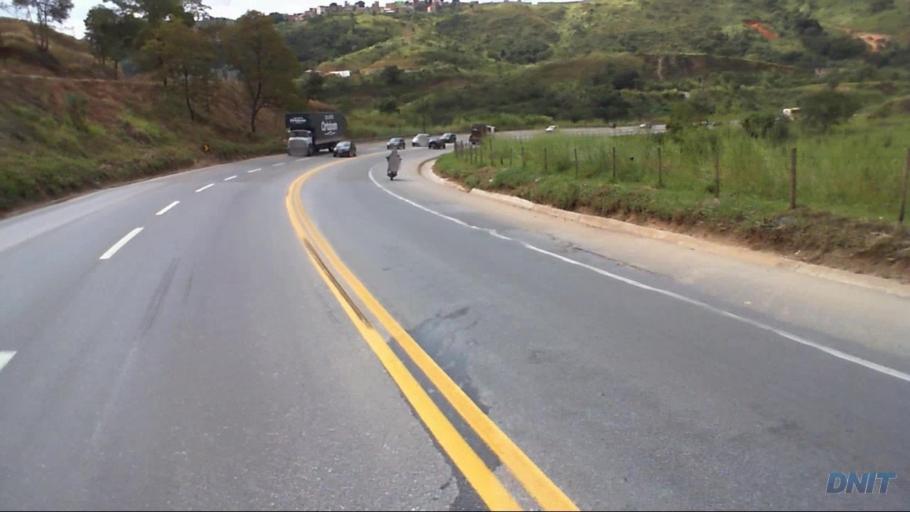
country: BR
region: Minas Gerais
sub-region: Santa Luzia
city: Santa Luzia
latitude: -19.8396
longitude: -43.8854
